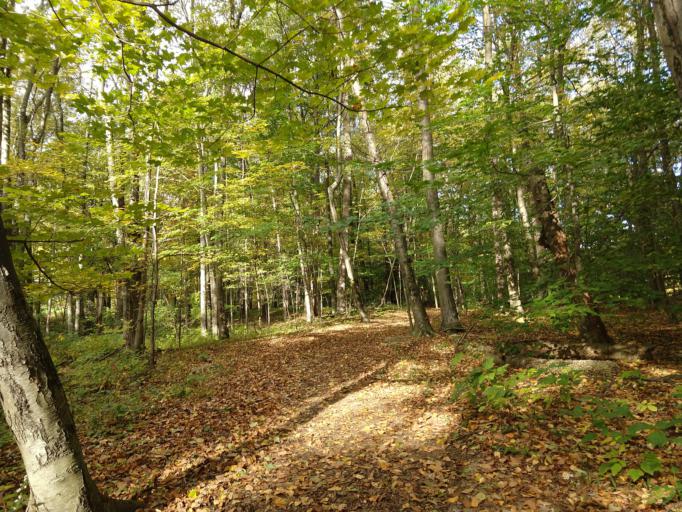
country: US
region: Connecticut
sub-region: Fairfield County
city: Georgetown
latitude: 41.2588
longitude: -73.4533
